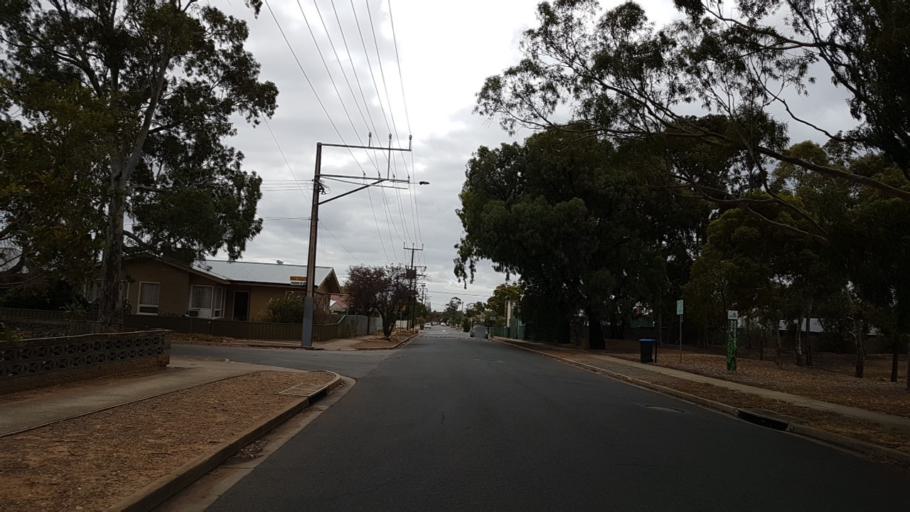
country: AU
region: South Australia
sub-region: Marion
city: Clovelly Park
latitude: -35.0012
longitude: 138.5695
